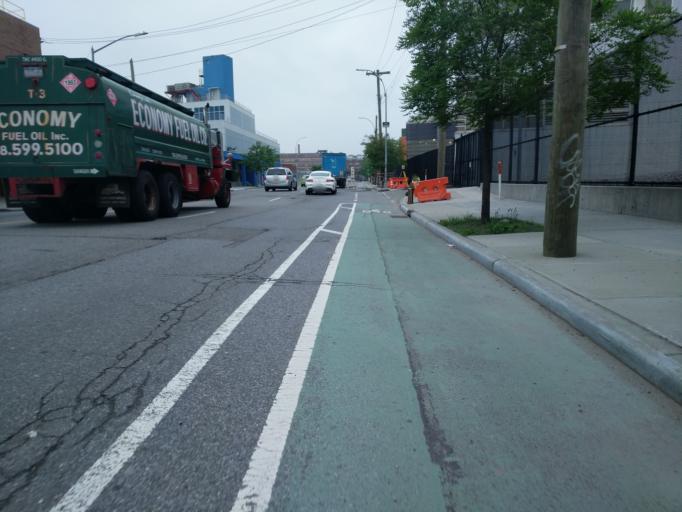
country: US
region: New York
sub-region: Queens County
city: Long Island City
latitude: 40.7323
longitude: -73.9443
